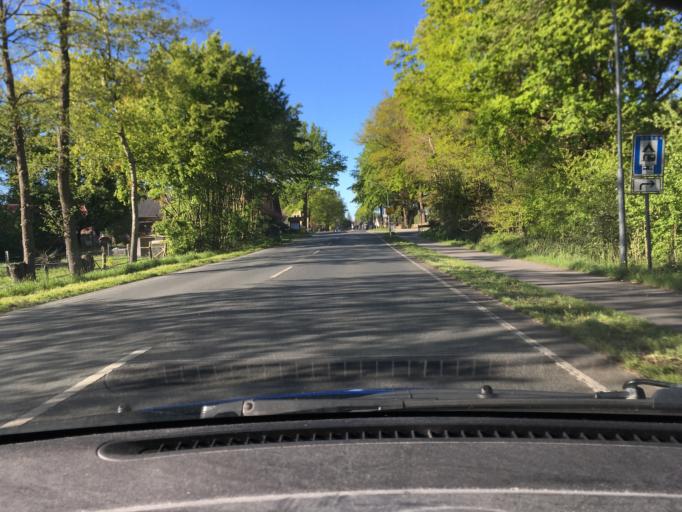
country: DE
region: Lower Saxony
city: Schneverdingen
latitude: 53.0706
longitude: 9.8623
